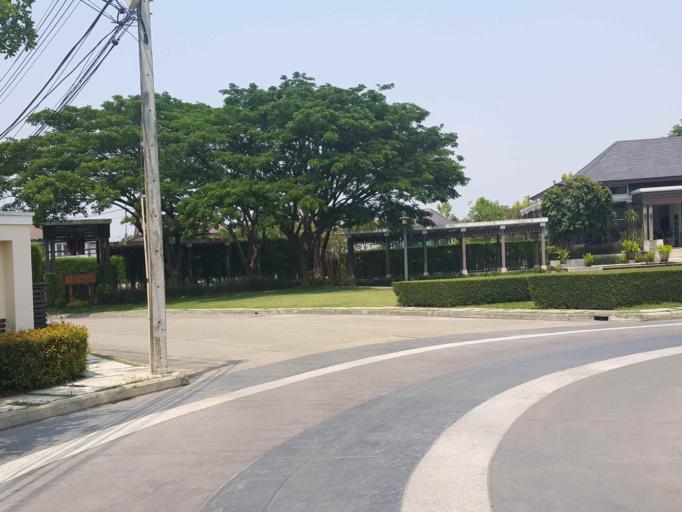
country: TH
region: Chiang Mai
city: Chiang Mai
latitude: 18.7482
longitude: 98.9521
